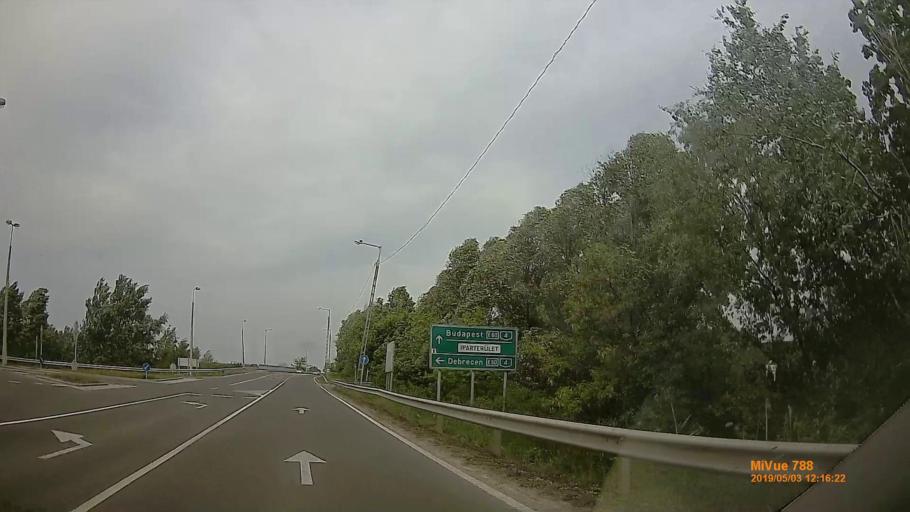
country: HU
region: Jasz-Nagykun-Szolnok
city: Szolnok
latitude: 47.1518
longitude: 20.2034
